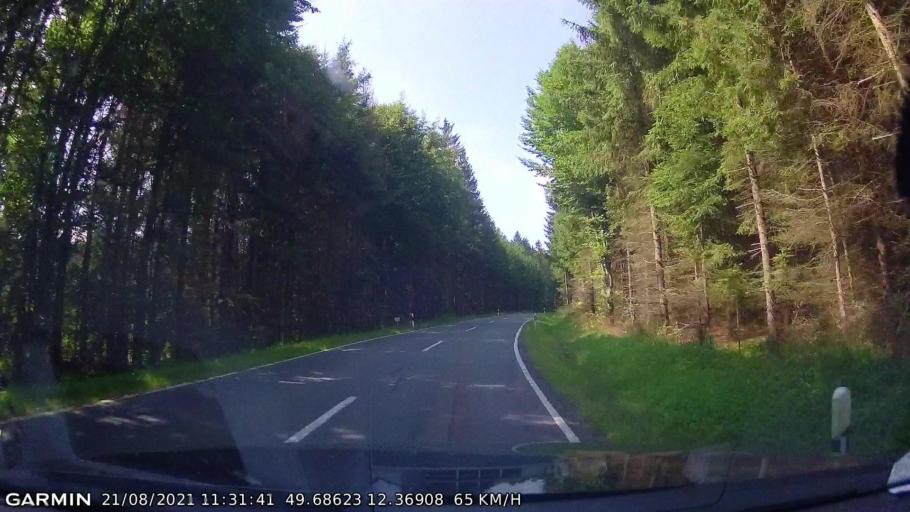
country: DE
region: Bavaria
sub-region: Upper Palatinate
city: Waldthurn
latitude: 49.6862
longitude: 12.3691
